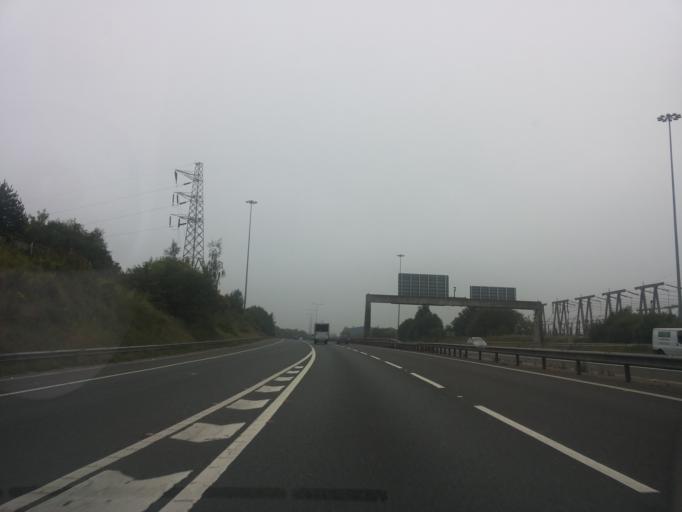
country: GB
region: England
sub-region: Manchester
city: Failsworth
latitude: 53.5279
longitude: -2.1654
